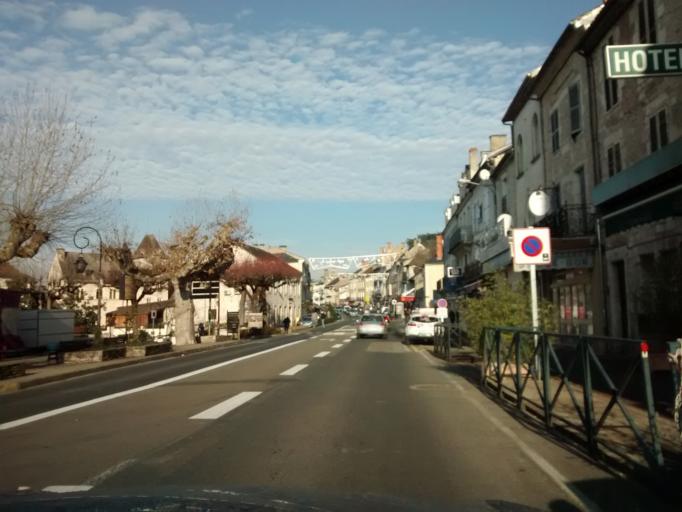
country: FR
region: Midi-Pyrenees
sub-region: Departement du Lot
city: Souillac
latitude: 44.8945
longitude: 1.4794
